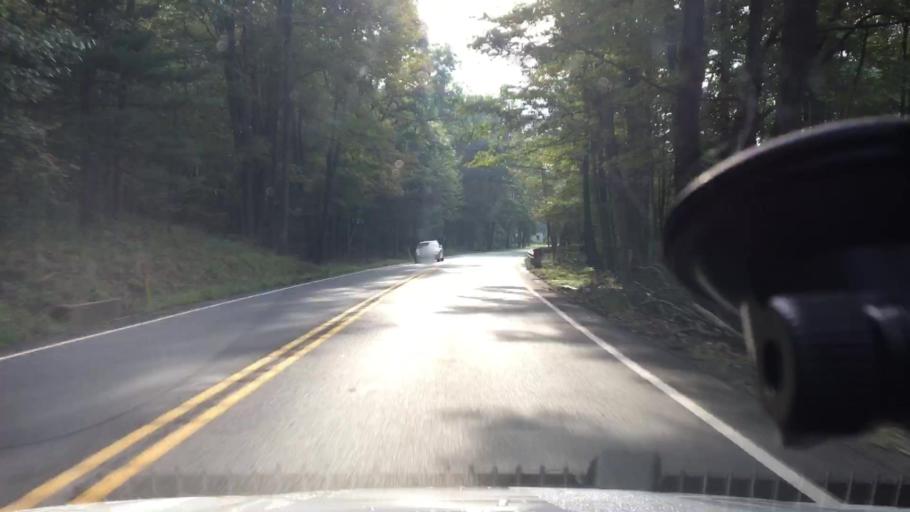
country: US
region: Pennsylvania
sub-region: Monroe County
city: Parkside
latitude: 41.1250
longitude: -75.2880
